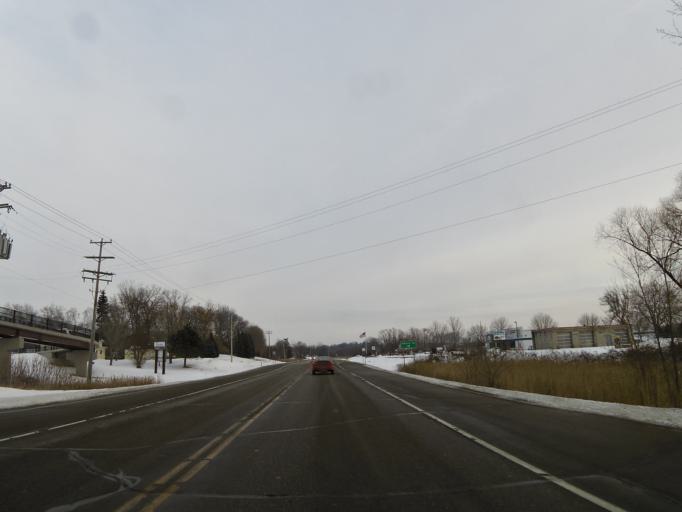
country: US
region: Minnesota
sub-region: Hennepin County
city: Saint Bonifacius
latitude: 44.9017
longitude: -93.7421
